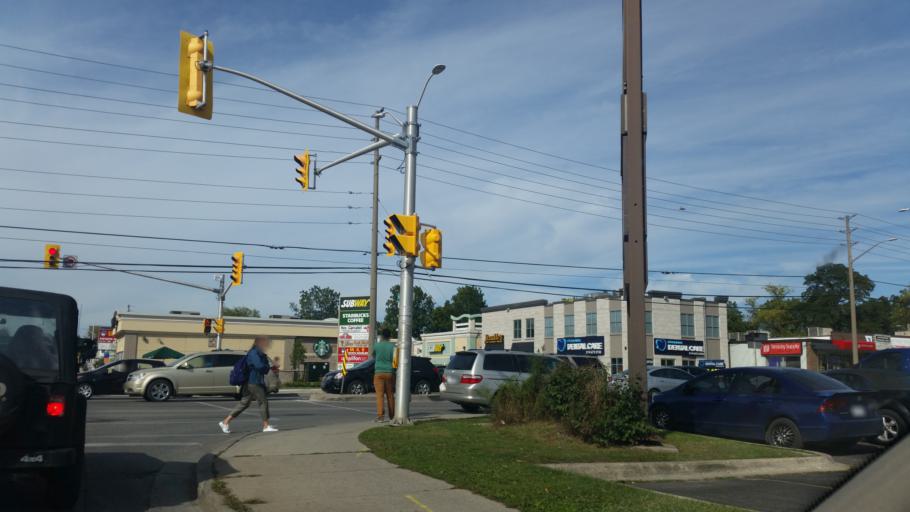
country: CA
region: Ontario
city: London
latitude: 42.9918
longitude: -81.2647
